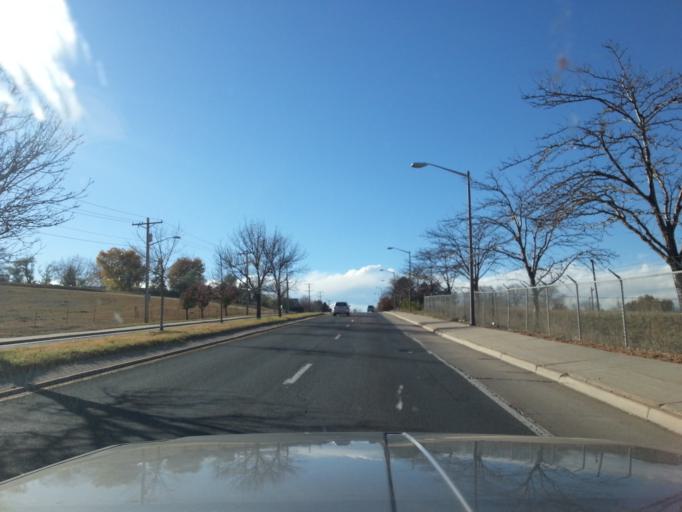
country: US
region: Colorado
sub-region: Larimer County
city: Loveland
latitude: 40.3784
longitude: -105.0853
